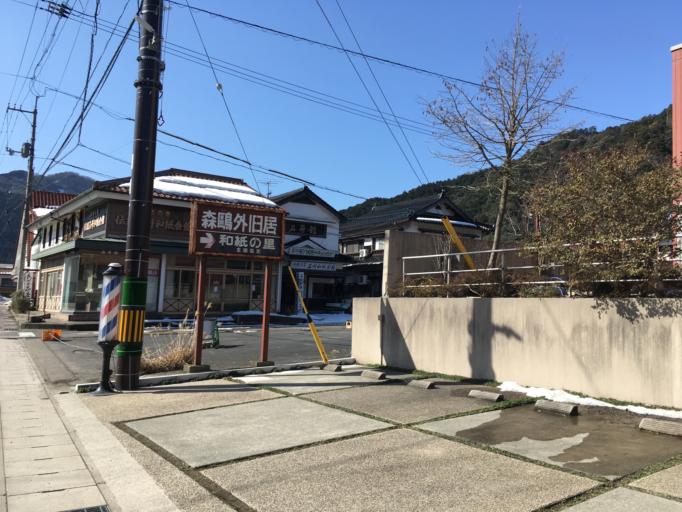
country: JP
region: Shimane
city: Masuda
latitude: 34.4579
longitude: 131.7693
